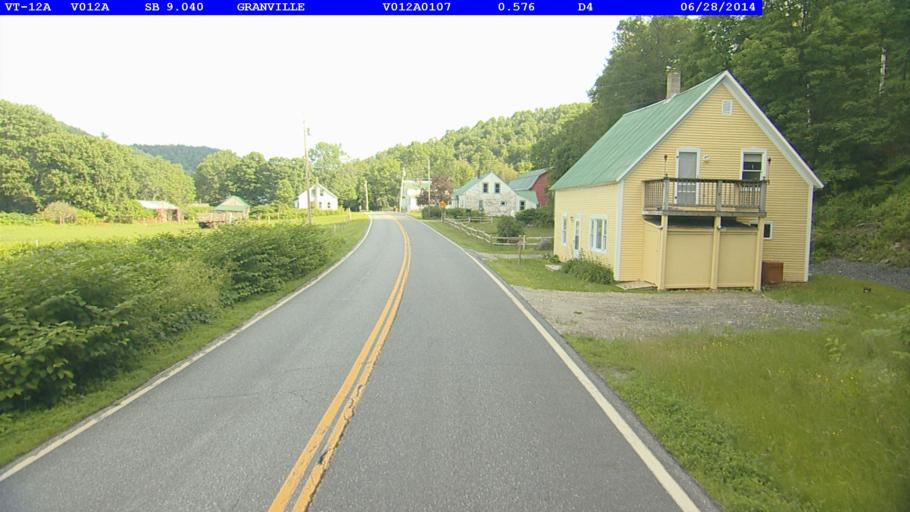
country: US
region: Vermont
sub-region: Orange County
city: Randolph
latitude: 44.0182
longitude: -72.7598
